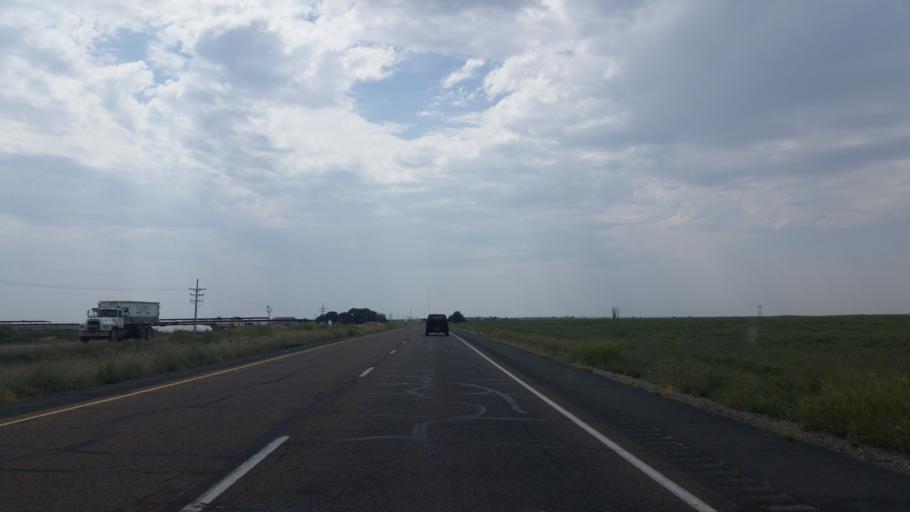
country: US
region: New Mexico
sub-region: Curry County
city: Clovis
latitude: 34.2908
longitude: -103.2074
